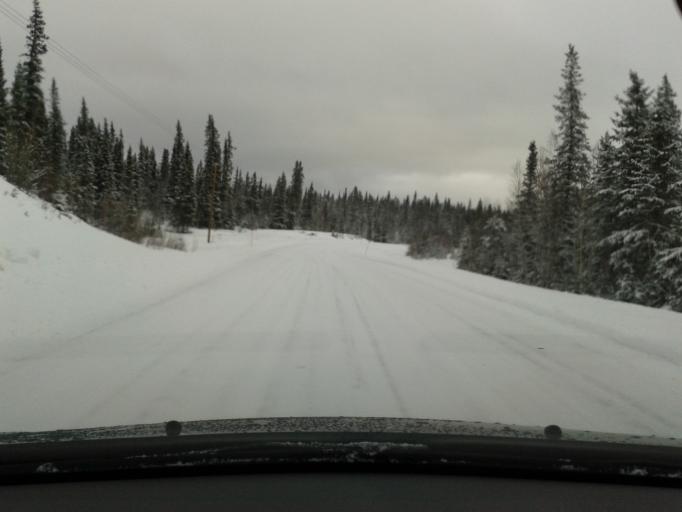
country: SE
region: Vaesterbotten
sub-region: Vilhelmina Kommun
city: Sjoberg
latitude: 65.2408
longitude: 15.7776
